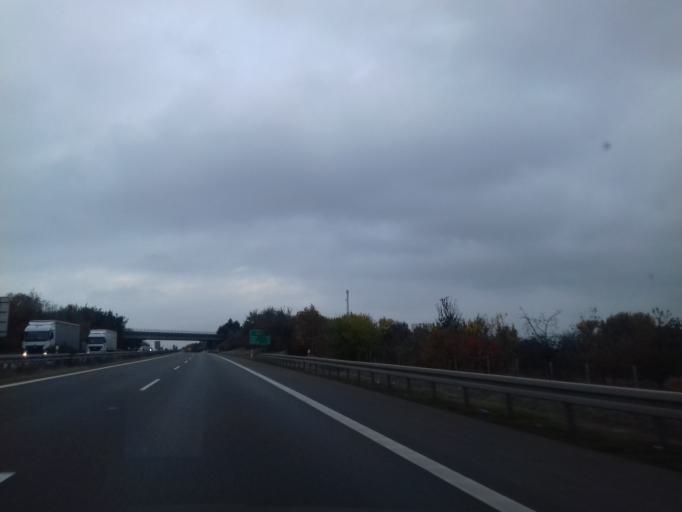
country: CZ
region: South Moravian
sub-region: Okres Breclav
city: Lanzhot
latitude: 48.7325
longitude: 16.9786
